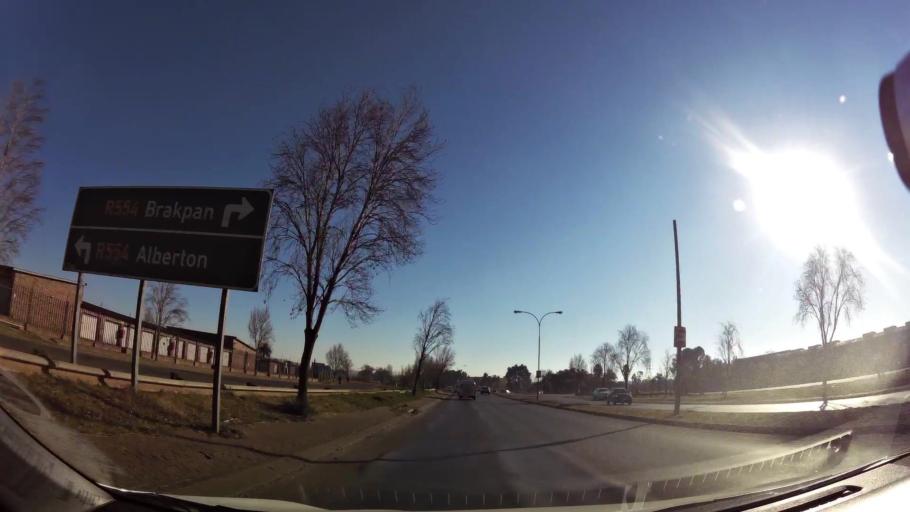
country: ZA
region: Gauteng
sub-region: Ekurhuleni Metropolitan Municipality
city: Germiston
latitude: -26.2911
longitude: 28.1378
